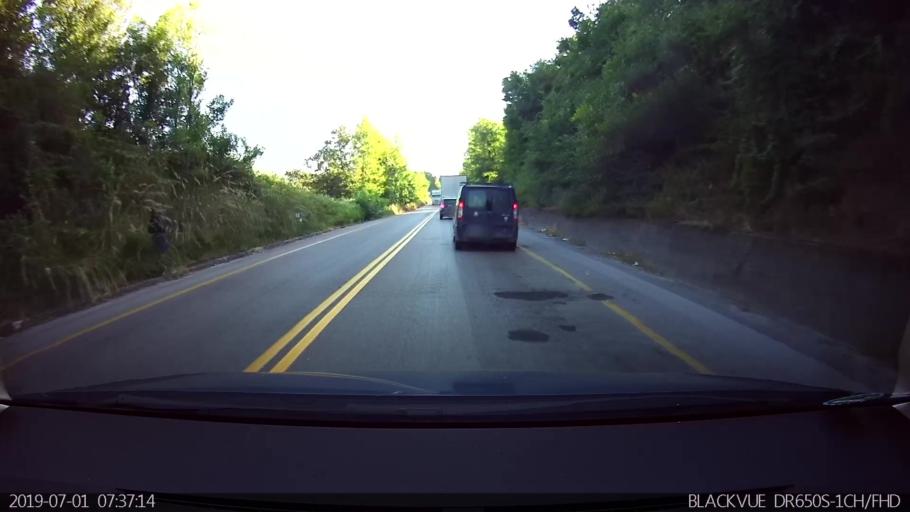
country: IT
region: Latium
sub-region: Provincia di Frosinone
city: Giuliano di Roma
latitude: 41.5366
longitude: 13.2668
